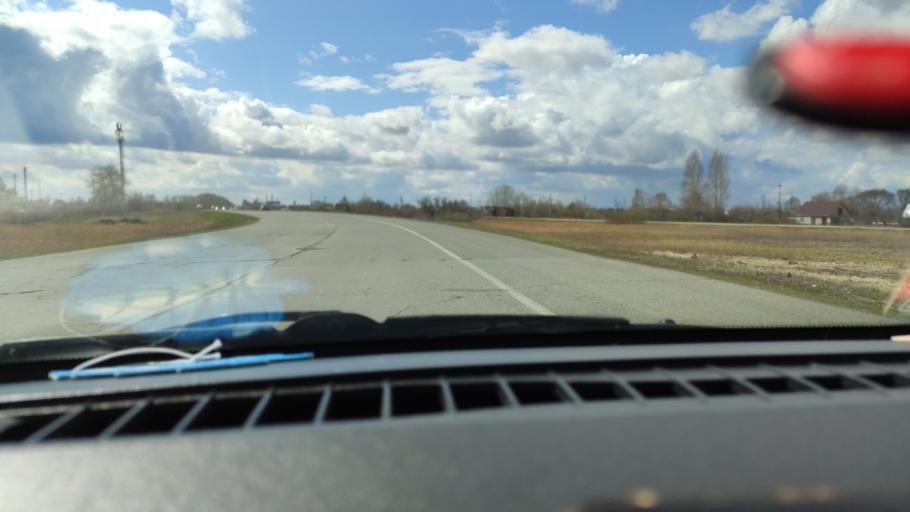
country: RU
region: Samara
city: Tol'yatti
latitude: 53.7123
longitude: 49.4238
